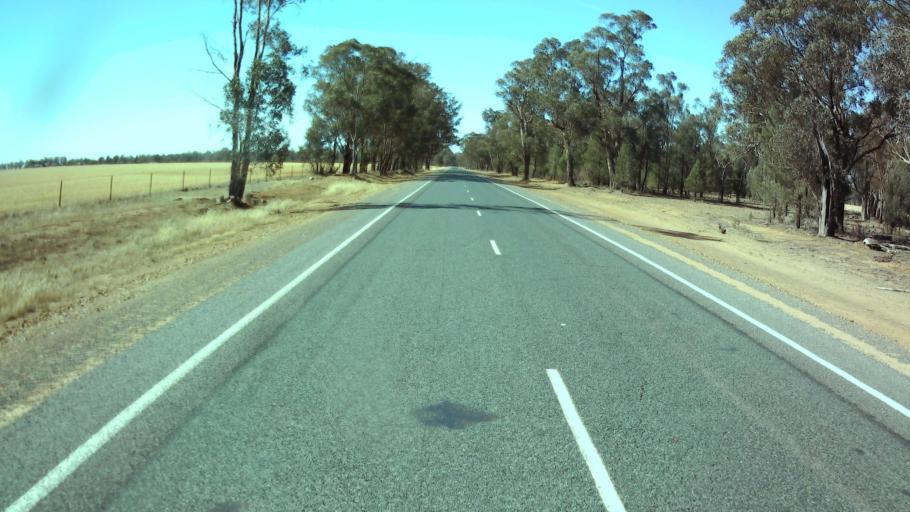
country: AU
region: New South Wales
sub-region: Weddin
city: Grenfell
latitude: -33.7398
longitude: 148.0887
